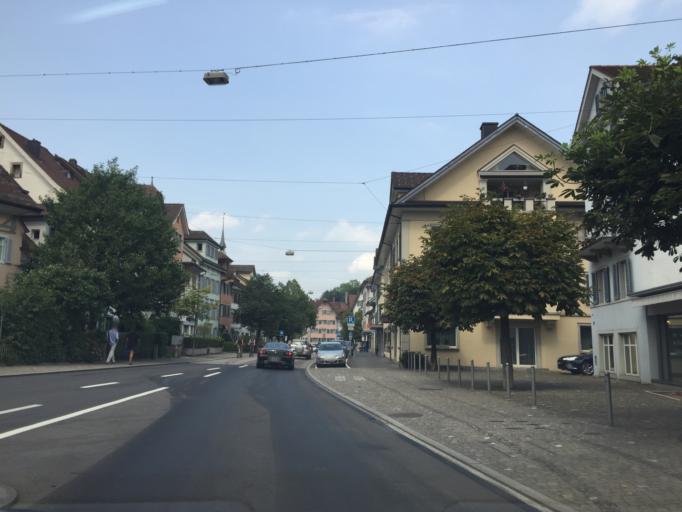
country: CH
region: Zug
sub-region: Zug
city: Zug
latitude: 47.1646
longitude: 8.5146
